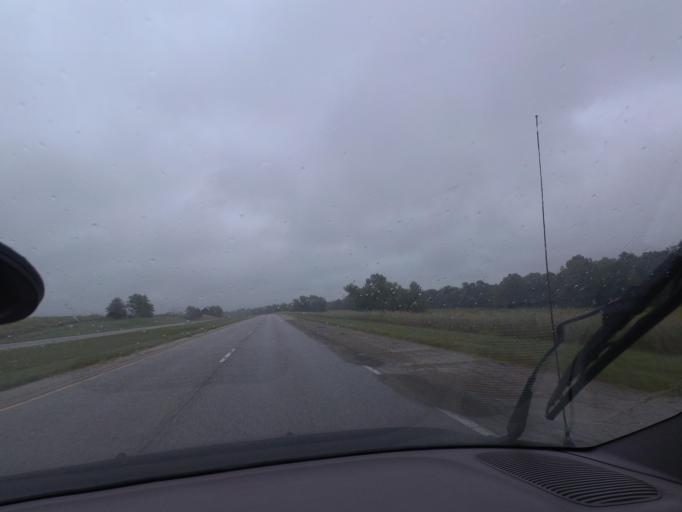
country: US
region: Illinois
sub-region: Pike County
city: Pittsfield
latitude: 39.6770
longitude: -90.8647
